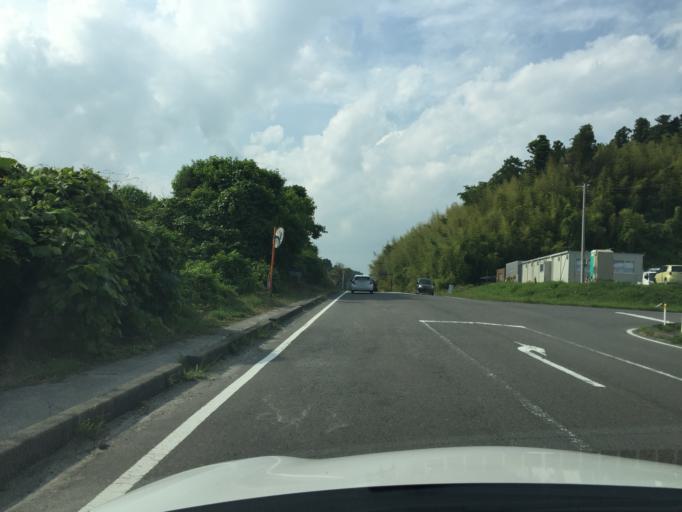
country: JP
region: Fukushima
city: Miharu
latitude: 37.4279
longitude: 140.4468
